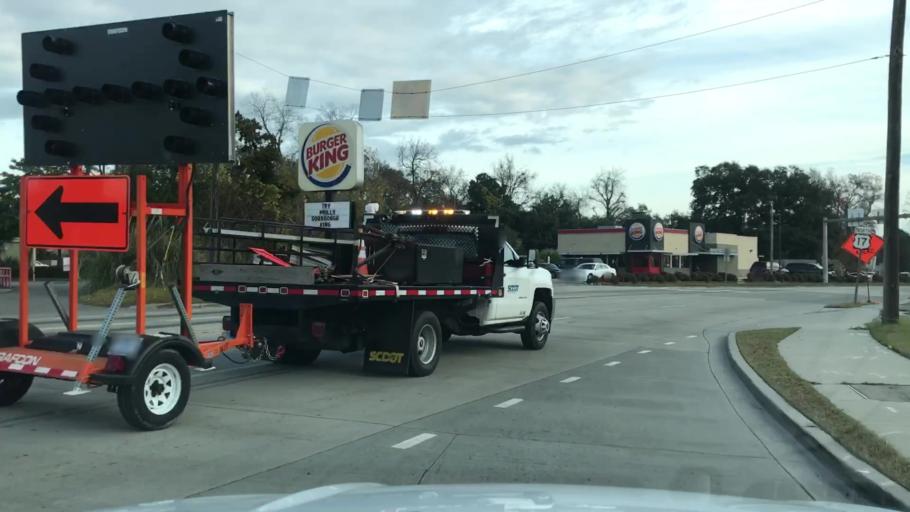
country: US
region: South Carolina
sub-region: Georgetown County
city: Georgetown
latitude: 33.3752
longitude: -79.2874
